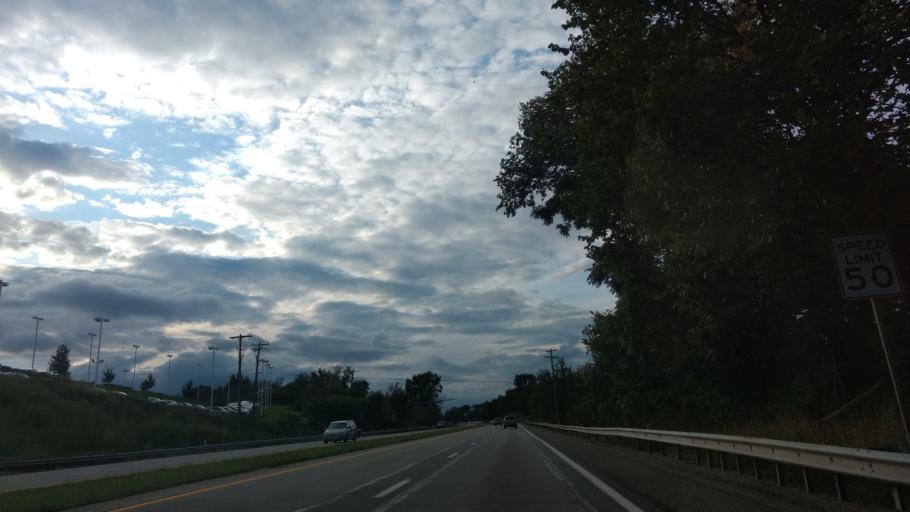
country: US
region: Pennsylvania
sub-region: Westmoreland County
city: Fellsburg
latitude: 40.1638
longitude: -79.7841
